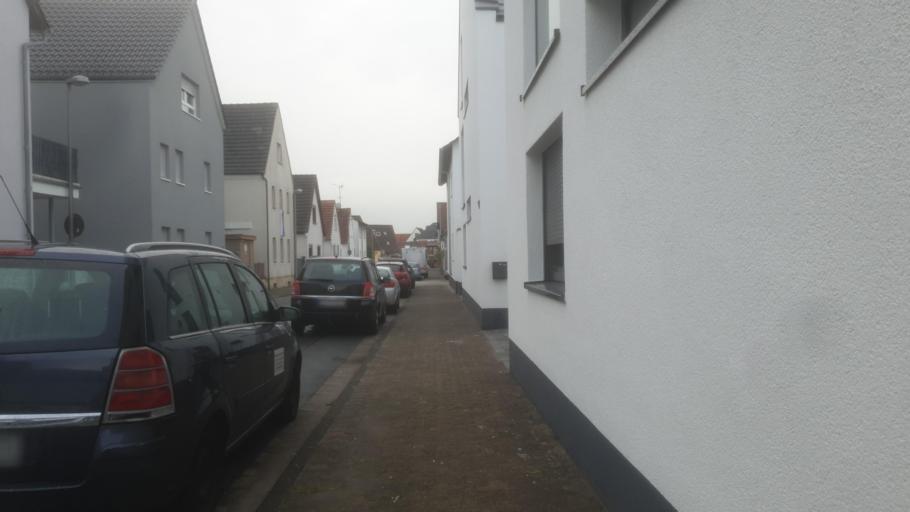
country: DE
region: Hesse
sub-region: Regierungsbezirk Darmstadt
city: Bischofsheim
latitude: 49.9617
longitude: 8.3802
